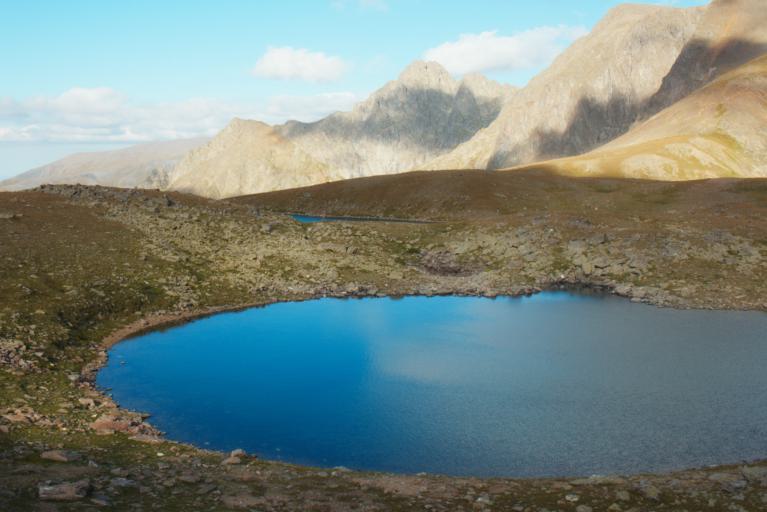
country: RU
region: Karachayevo-Cherkesiya
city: Mednogorskiy
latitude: 43.6160
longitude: 41.1086
